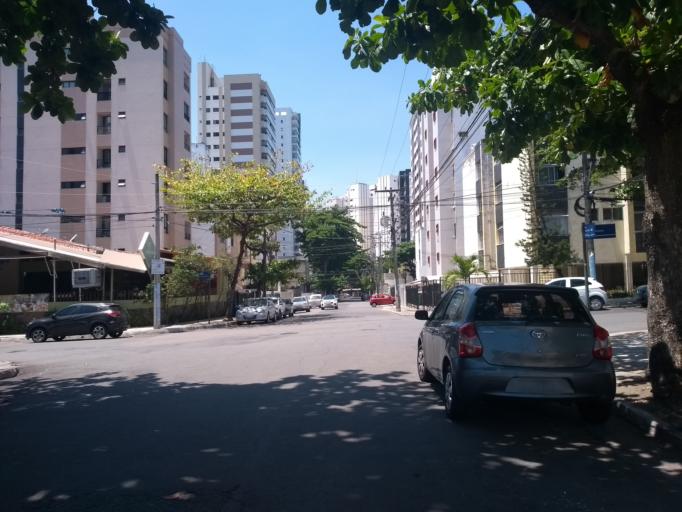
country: BR
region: Bahia
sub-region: Salvador
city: Salvador
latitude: -13.0001
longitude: -38.4570
